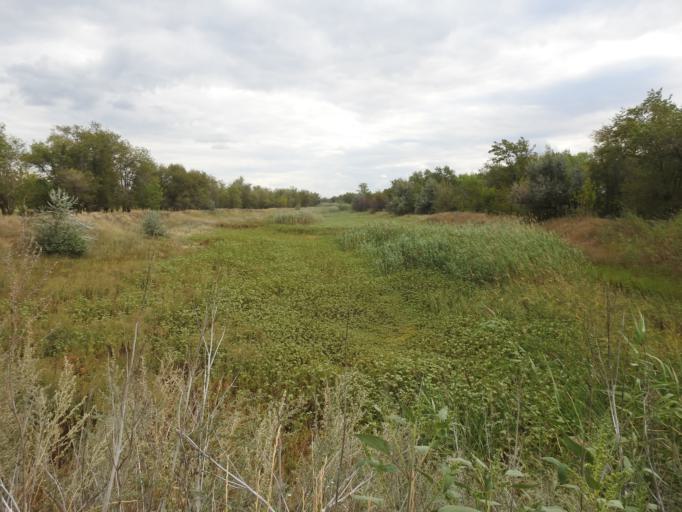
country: RU
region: Saratov
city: Shumeyka
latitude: 51.4395
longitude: 46.3058
